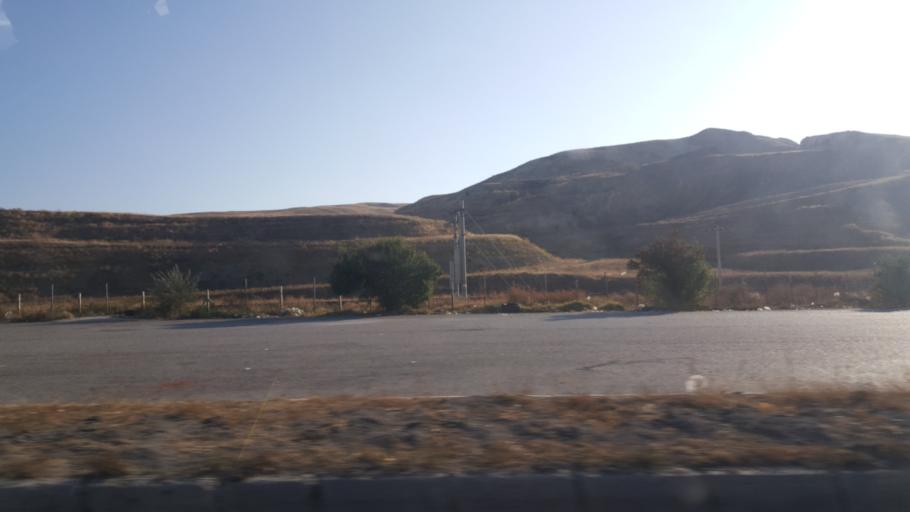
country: TR
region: Ankara
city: Polatli
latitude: 39.5752
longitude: 32.0745
